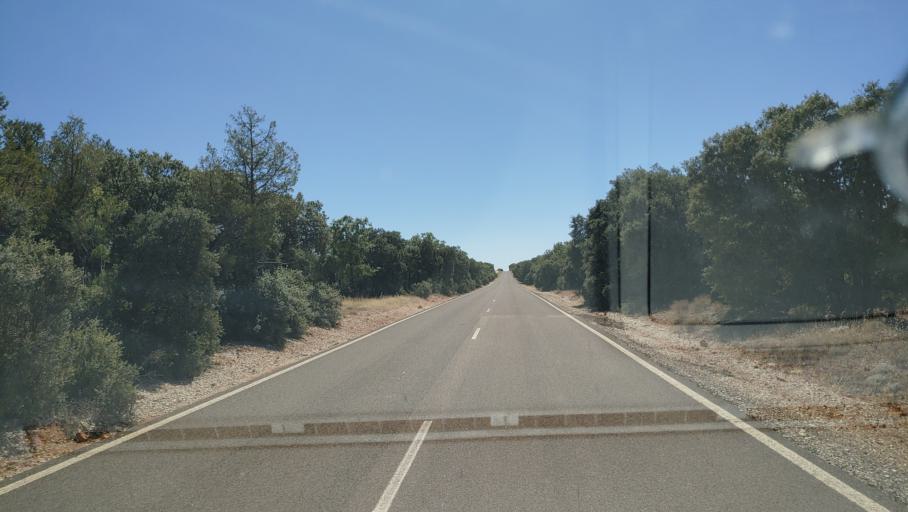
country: ES
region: Castille-La Mancha
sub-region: Provincia de Ciudad Real
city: Villahermosa
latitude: 38.8172
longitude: -2.8325
